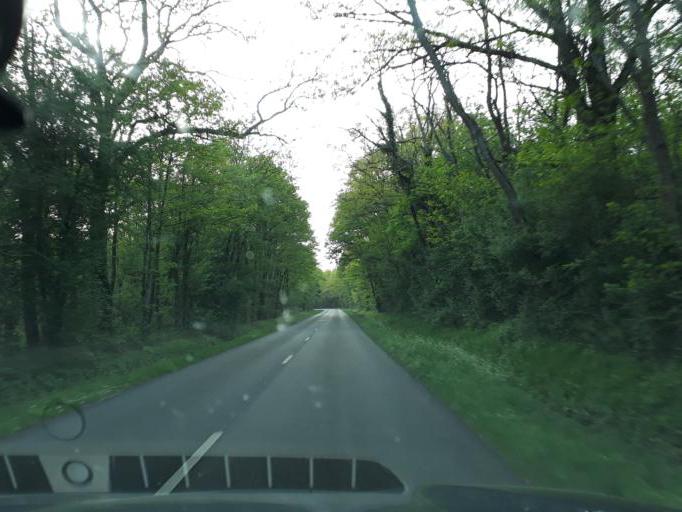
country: FR
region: Centre
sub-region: Departement du Loir-et-Cher
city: Muides-sur-Loire
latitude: 47.6500
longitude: 1.5889
